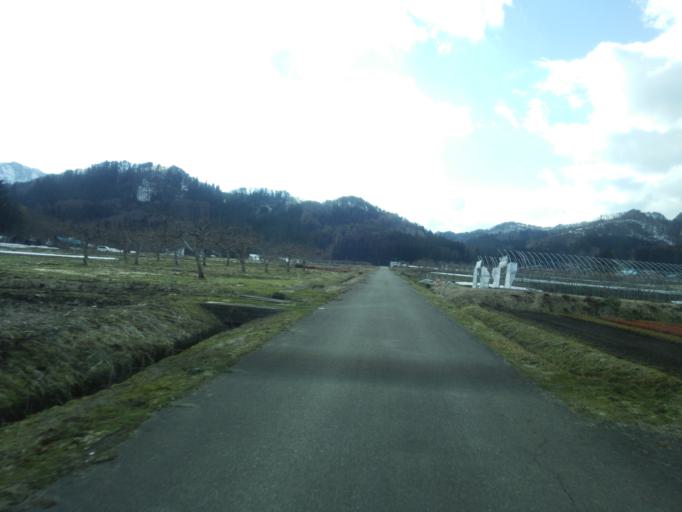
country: JP
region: Fukushima
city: Kitakata
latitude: 37.4479
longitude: 139.8052
